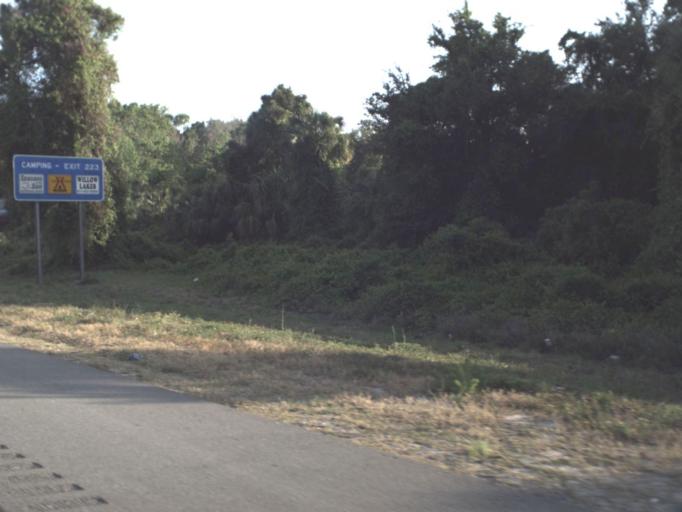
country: US
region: Florida
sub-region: Brevard County
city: Mims
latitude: 28.6749
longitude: -80.8734
